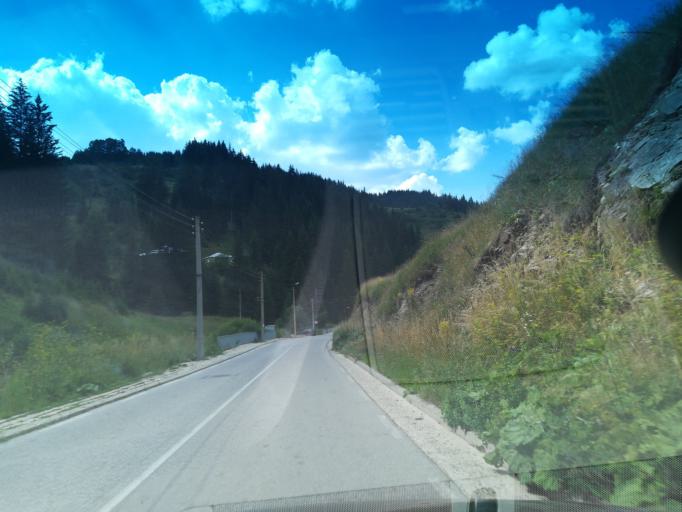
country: BG
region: Smolyan
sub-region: Obshtina Smolyan
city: Smolyan
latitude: 41.6562
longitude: 24.6340
